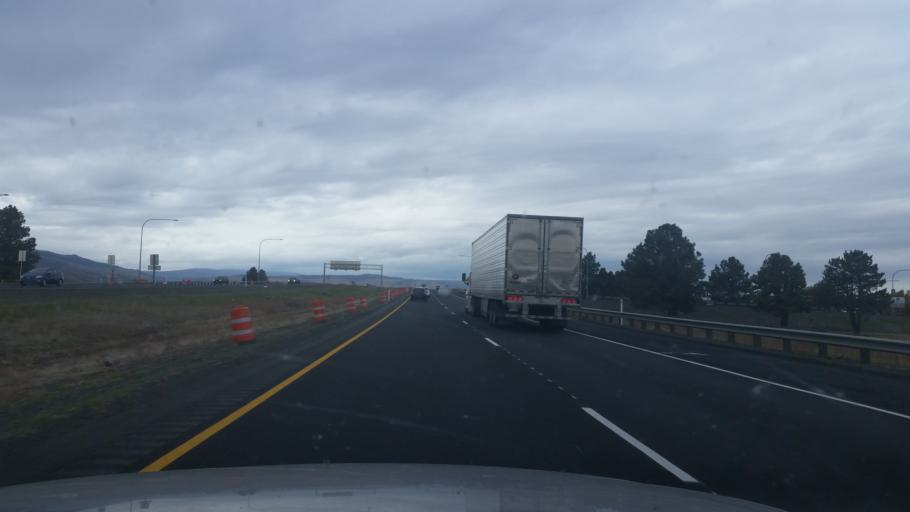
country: US
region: Washington
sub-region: Kittitas County
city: Ellensburg
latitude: 46.9729
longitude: -120.5358
